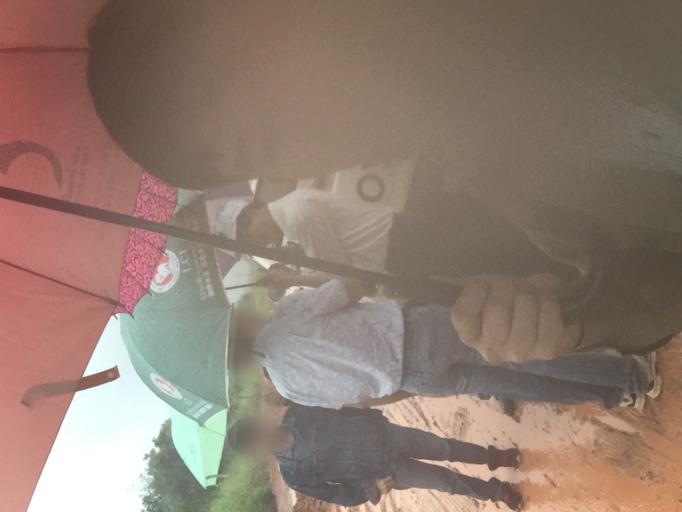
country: LA
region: Bolikhamxai
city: Bolikhan
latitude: 18.5095
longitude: 103.8432
